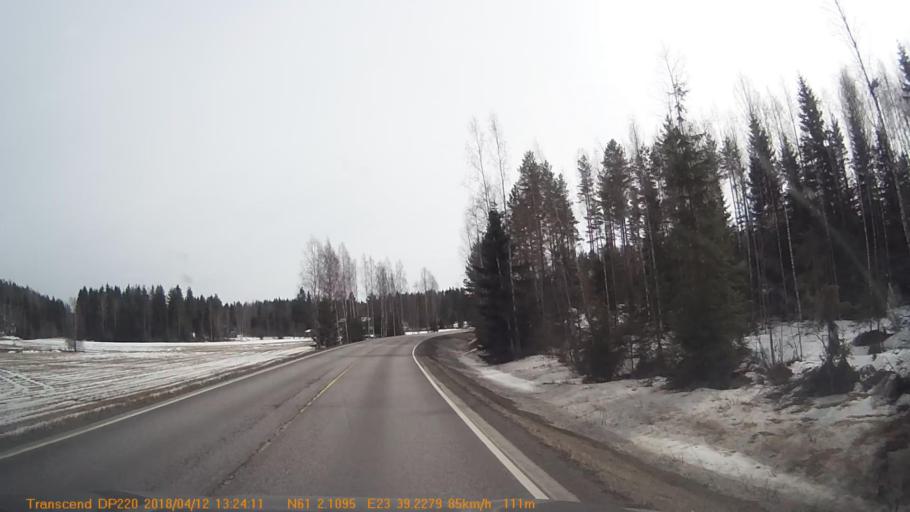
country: FI
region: Pirkanmaa
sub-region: Etelae-Pirkanmaa
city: Kylmaekoski
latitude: 61.0342
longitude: 23.6550
